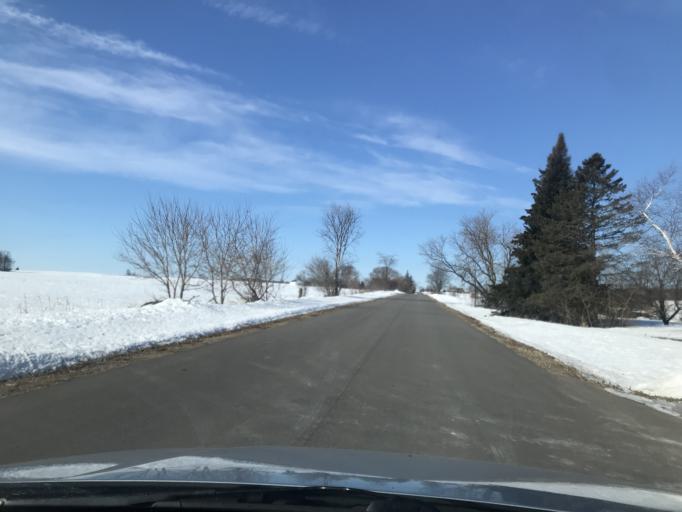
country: US
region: Wisconsin
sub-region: Oconto County
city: Gillett
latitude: 44.9396
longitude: -88.2593
